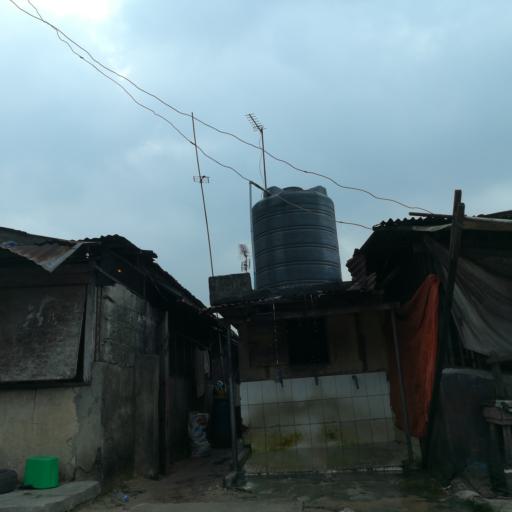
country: NG
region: Rivers
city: Port Harcourt
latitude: 4.8083
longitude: 7.0493
